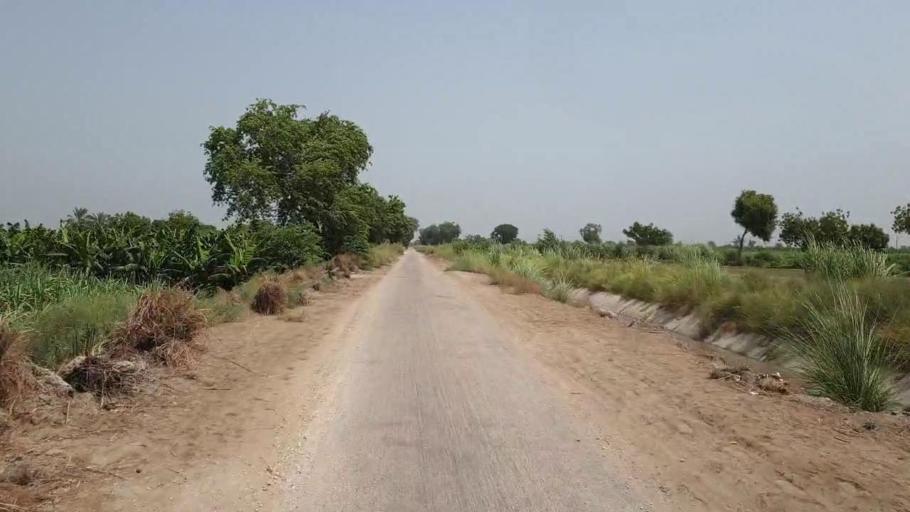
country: PK
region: Sindh
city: Nawabshah
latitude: 26.2797
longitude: 68.3123
